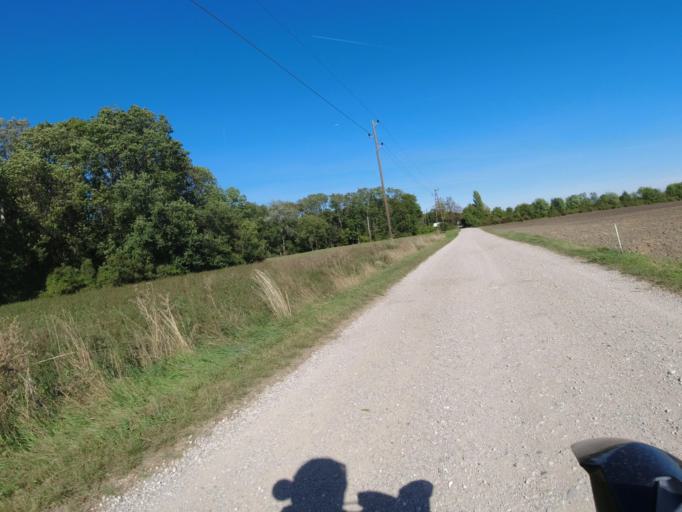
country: AT
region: Lower Austria
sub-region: Politischer Bezirk Modling
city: Guntramsdorf
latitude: 48.0241
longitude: 16.3234
